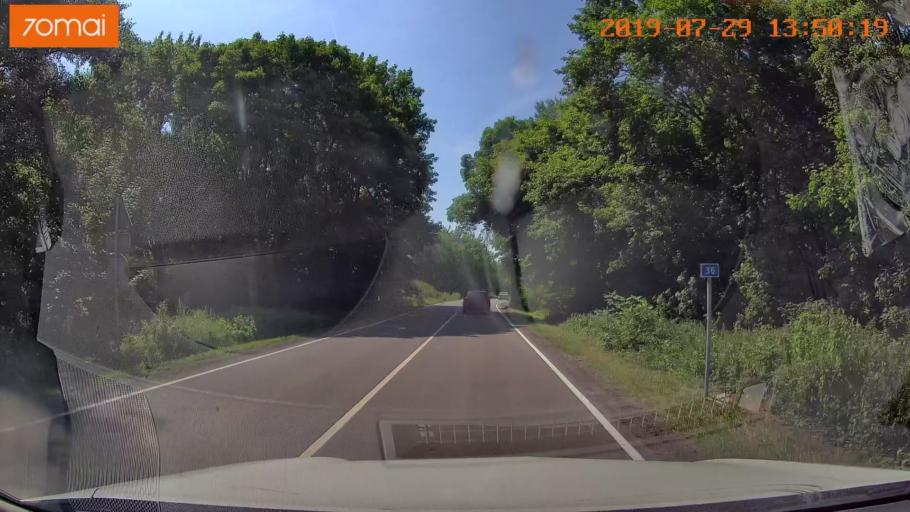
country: RU
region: Kaliningrad
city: Primorsk
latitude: 54.7296
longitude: 20.0157
